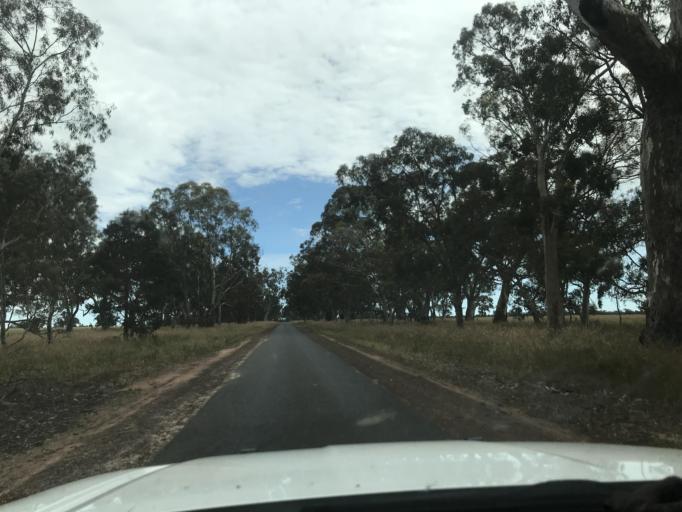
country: AU
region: Victoria
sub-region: Horsham
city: Horsham
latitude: -37.0343
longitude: 141.5693
